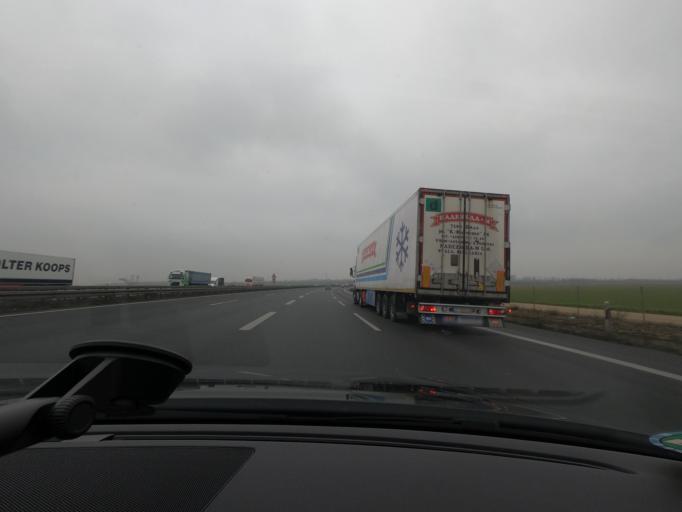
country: DE
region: North Rhine-Westphalia
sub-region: Regierungsbezirk Dusseldorf
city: Juchen
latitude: 51.0826
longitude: 6.4769
